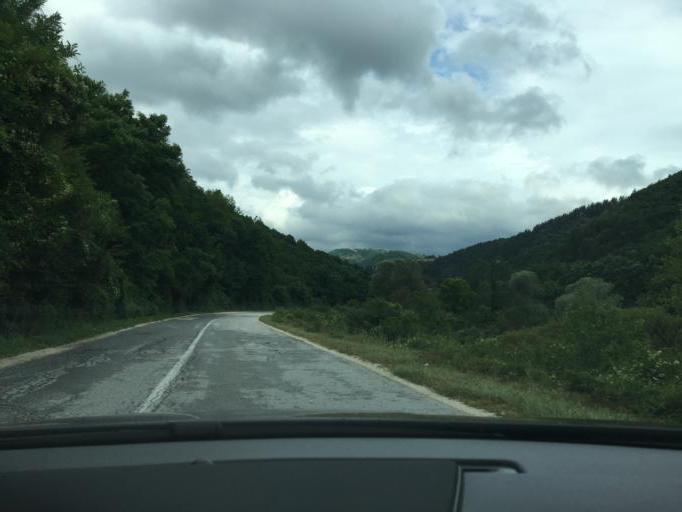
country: MK
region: Kriva Palanka
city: Kriva Palanka
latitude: 42.2264
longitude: 22.3866
